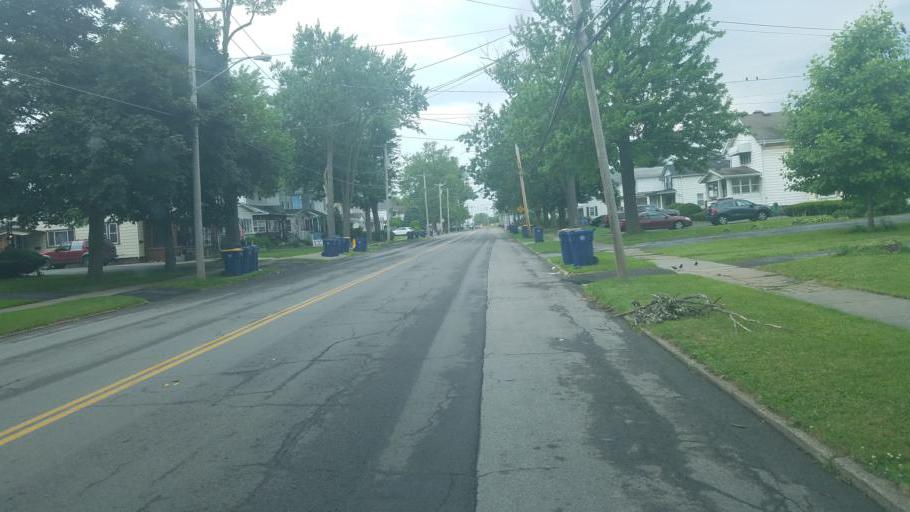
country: US
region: New York
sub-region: Niagara County
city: Lockport
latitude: 43.1689
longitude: -78.7029
